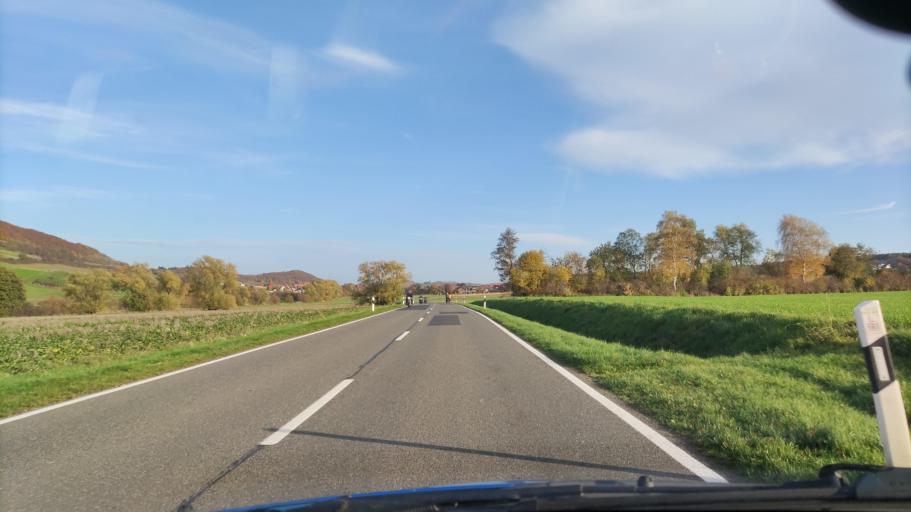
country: DE
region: Lower Saxony
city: Dassel
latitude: 51.7756
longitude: 9.6993
